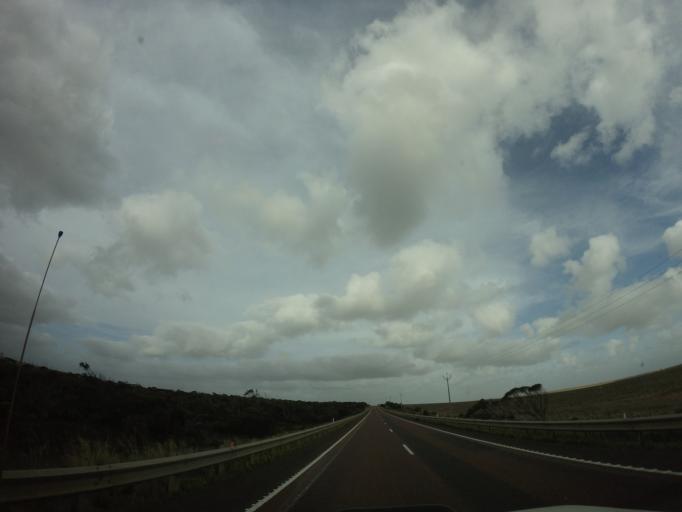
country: AU
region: South Australia
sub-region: Ceduna
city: Ceduna
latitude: -32.0663
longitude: 133.6302
